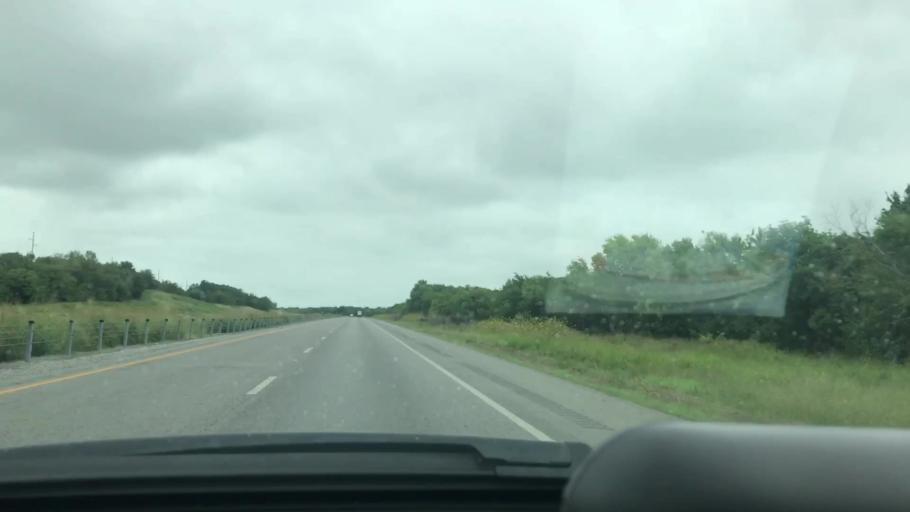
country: US
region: Oklahoma
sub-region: Coal County
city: Coalgate
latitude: 34.6409
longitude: -95.9488
